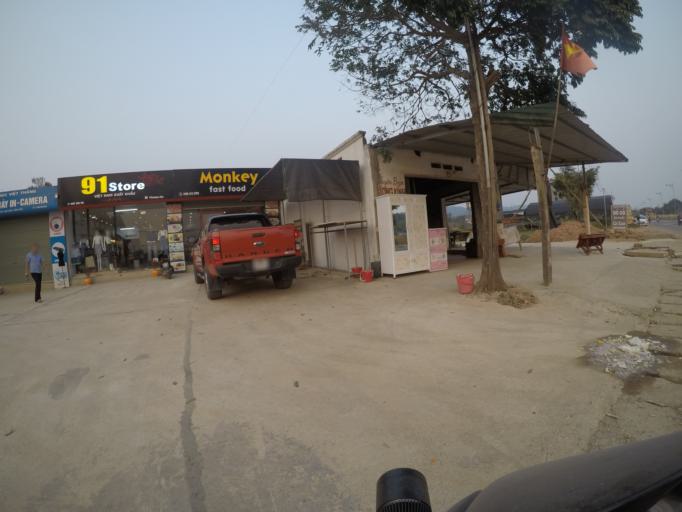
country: VN
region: Vinh Phuc
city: Trai Ngau
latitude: 21.4291
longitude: 105.5883
